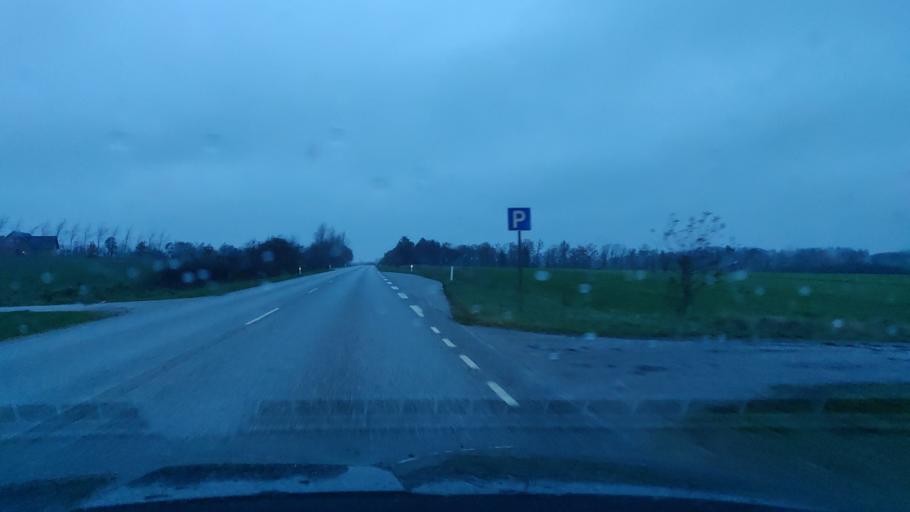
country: DK
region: Central Jutland
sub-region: Herning Kommune
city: Avlum
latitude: 56.2723
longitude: 8.7641
